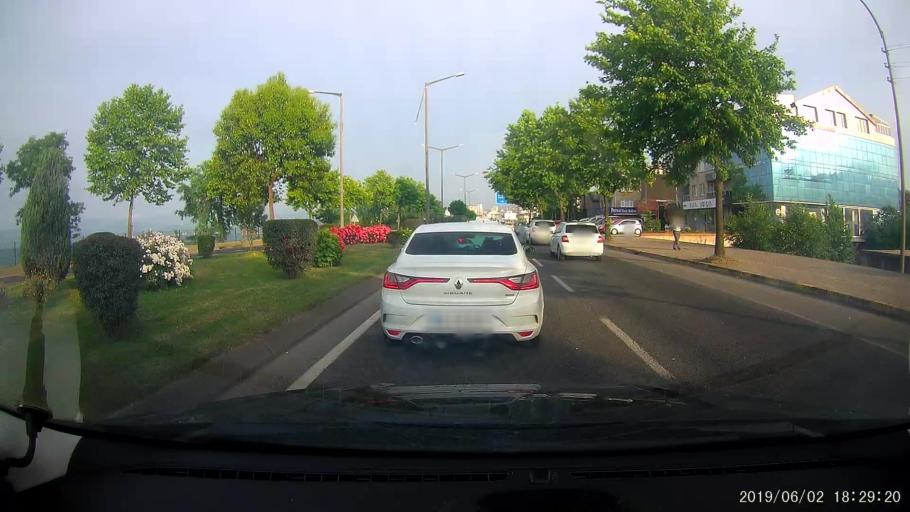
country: TR
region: Ordu
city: Fatsa
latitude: 41.0390
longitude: 37.4902
